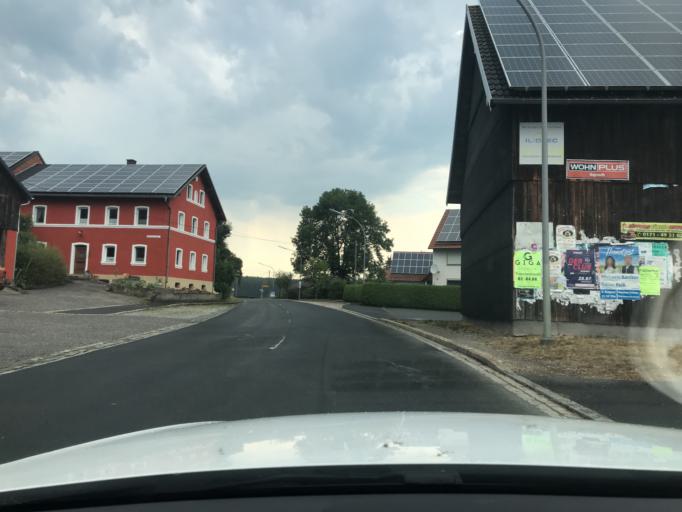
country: DE
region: Bavaria
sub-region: Upper Palatinate
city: Vorbach
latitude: 49.7922
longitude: 11.7664
